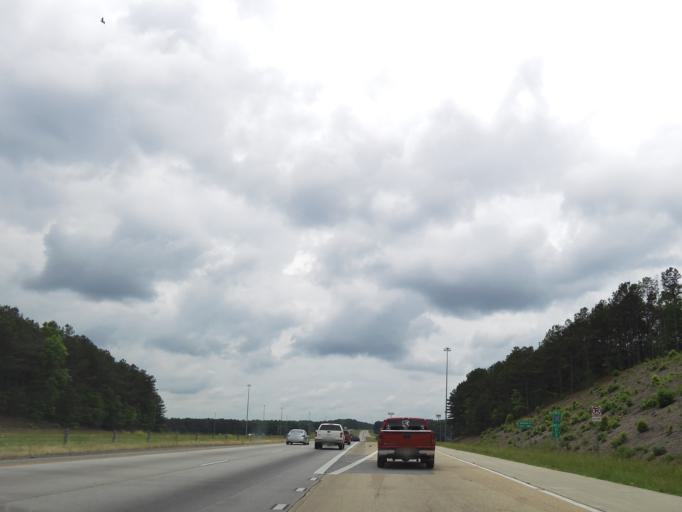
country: US
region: Georgia
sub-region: Haralson County
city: Bremen
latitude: 33.6856
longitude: -85.1456
